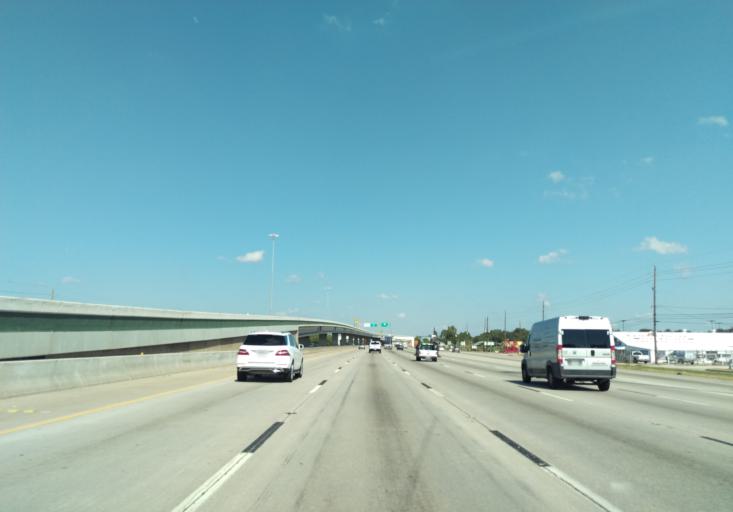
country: US
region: Texas
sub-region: Harris County
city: Spring
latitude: 30.0084
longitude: -95.4272
